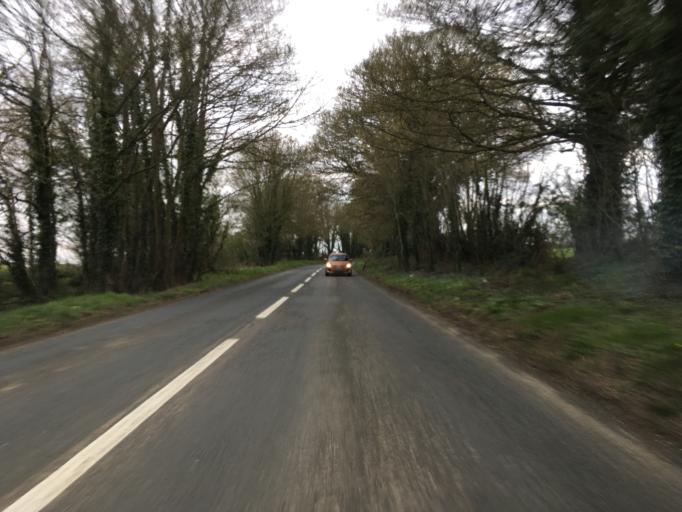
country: GB
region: England
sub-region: Gloucestershire
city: Northleach
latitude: 51.7541
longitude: -1.8547
